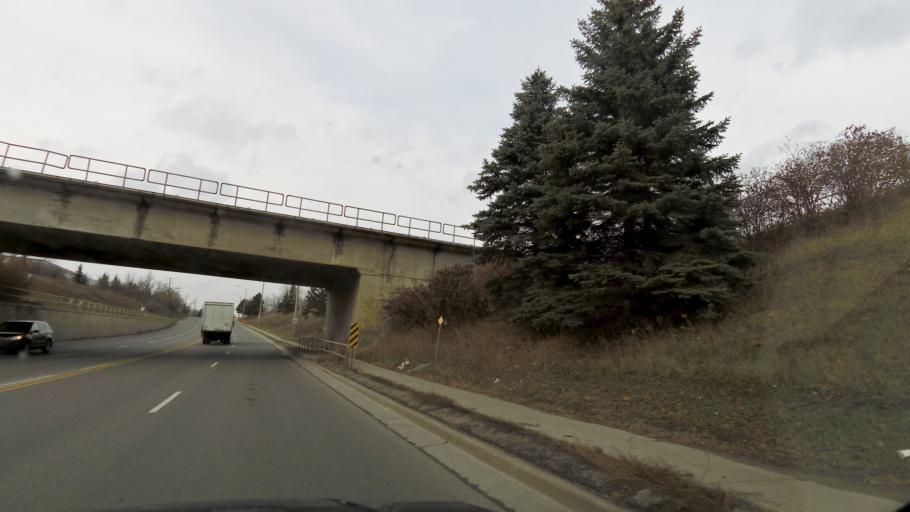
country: CA
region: Ontario
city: Etobicoke
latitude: 43.7371
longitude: -79.6389
